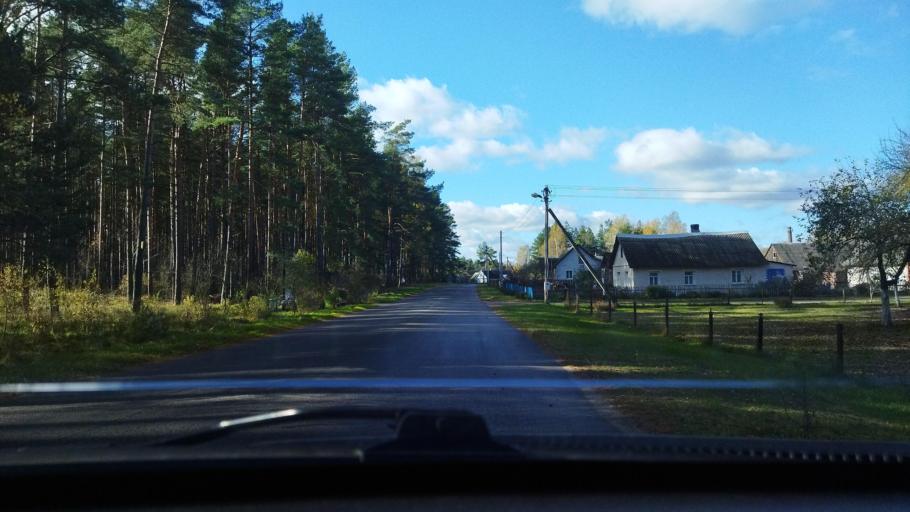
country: BY
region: Minsk
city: Svir
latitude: 54.8038
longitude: 26.2418
